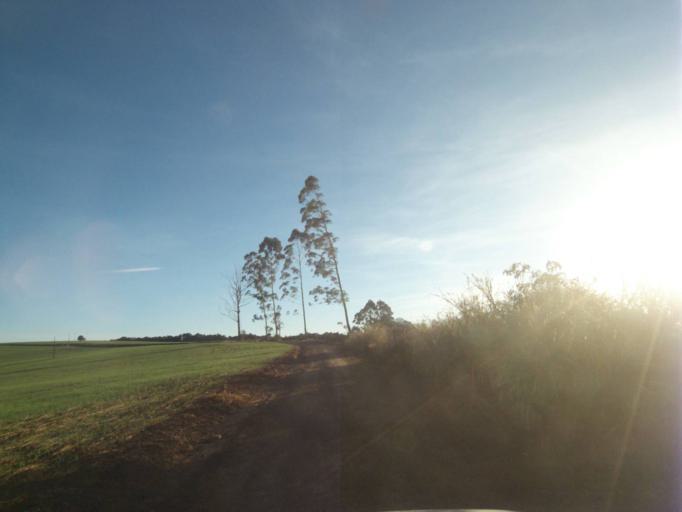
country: BR
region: Parana
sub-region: Telemaco Borba
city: Telemaco Borba
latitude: -24.4803
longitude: -50.5917
